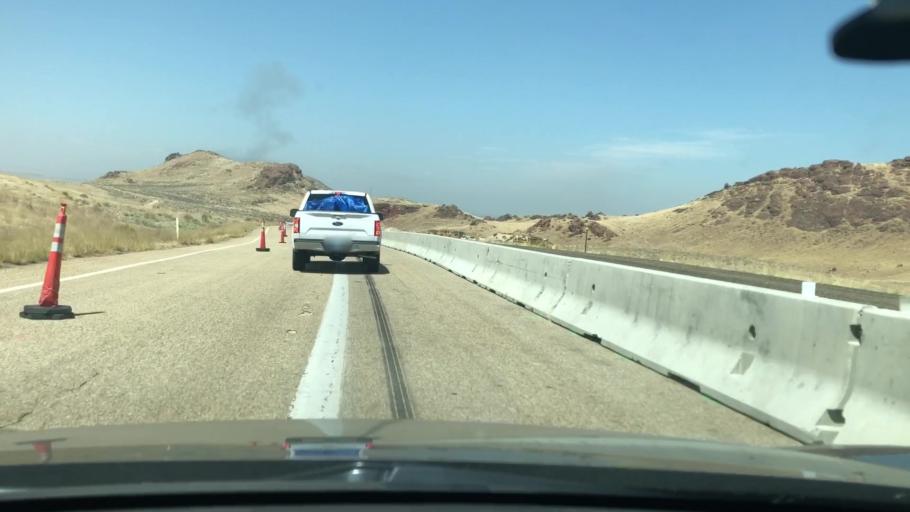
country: US
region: Idaho
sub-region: Owyhee County
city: Marsing
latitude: 43.4545
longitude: -116.8618
